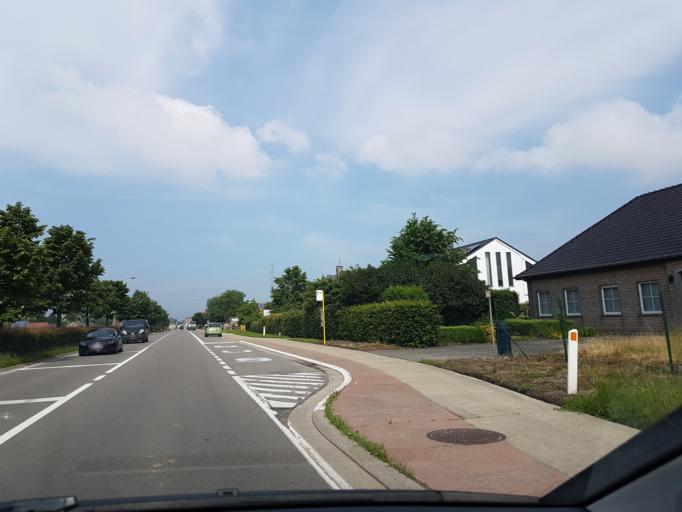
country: BE
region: Flanders
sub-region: Provincie Vlaams-Brabant
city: Merchtem
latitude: 50.9566
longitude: 4.2514
